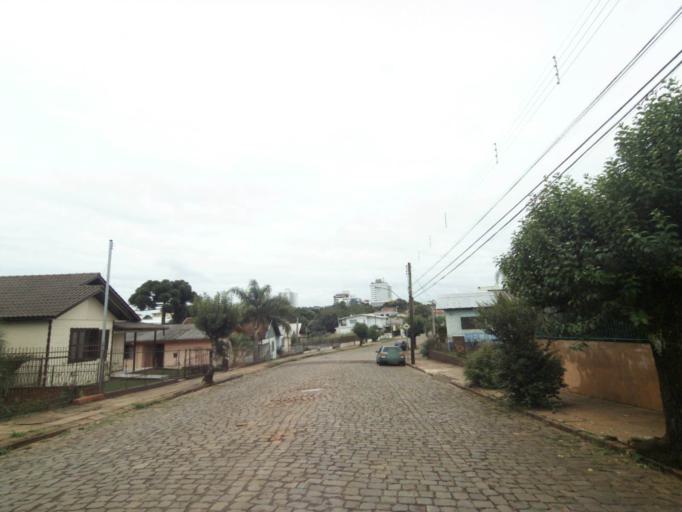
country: BR
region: Rio Grande do Sul
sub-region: Lagoa Vermelha
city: Lagoa Vermelha
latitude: -28.2160
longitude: -51.5214
